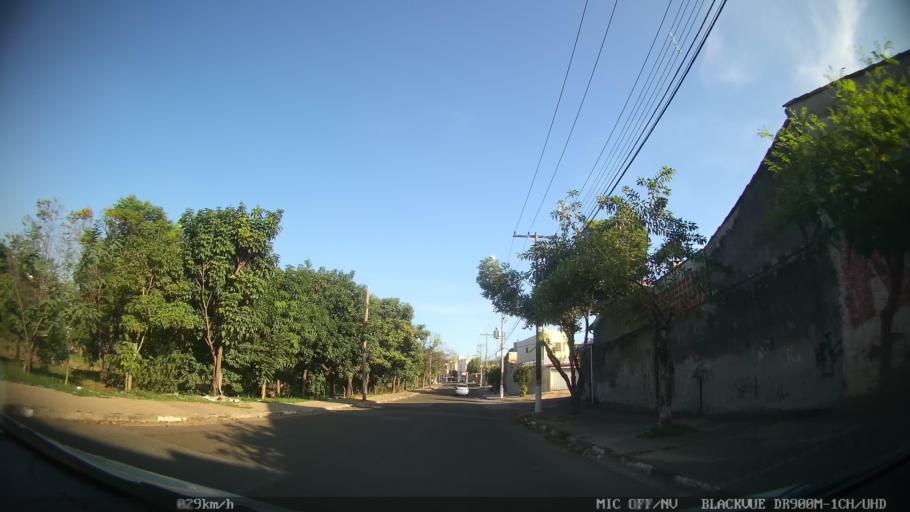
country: BR
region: Sao Paulo
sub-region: Campinas
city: Campinas
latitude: -22.9760
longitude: -47.1257
